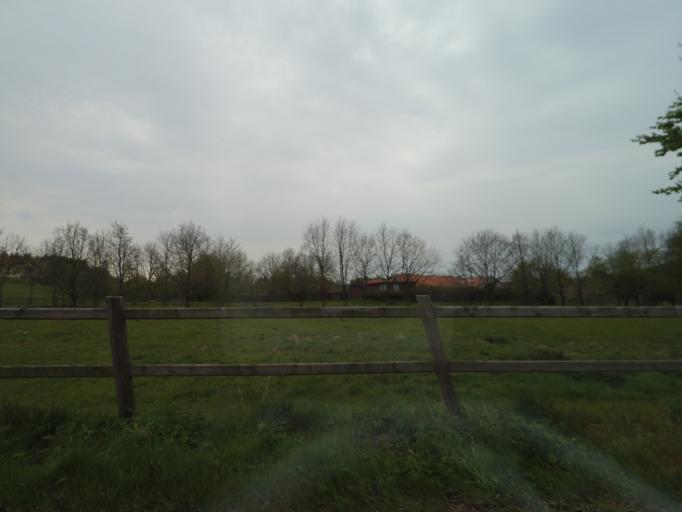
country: DK
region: South Denmark
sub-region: Svendborg Kommune
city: Thuro By
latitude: 55.1566
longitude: 10.6923
